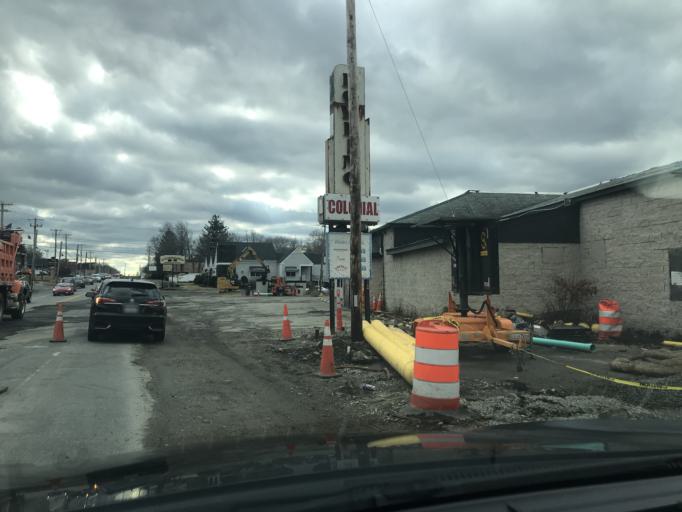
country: US
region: Massachusetts
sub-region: Plymouth County
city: Rockland
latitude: 42.1685
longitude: -70.9554
